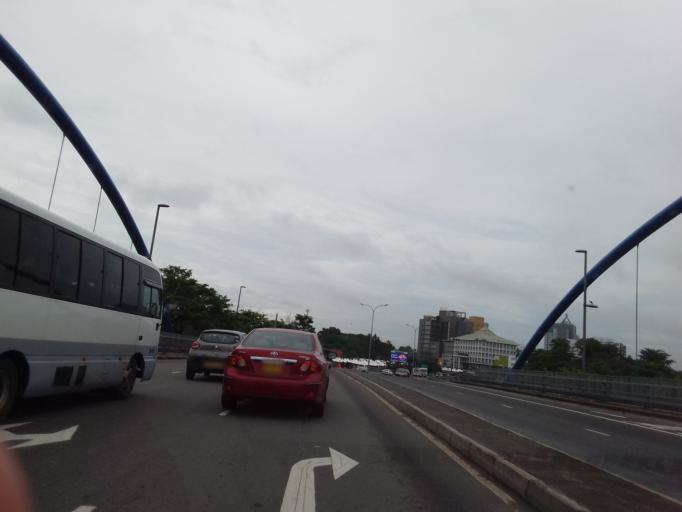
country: LK
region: Western
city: Battaramulla South
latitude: 6.9031
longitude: 79.9086
